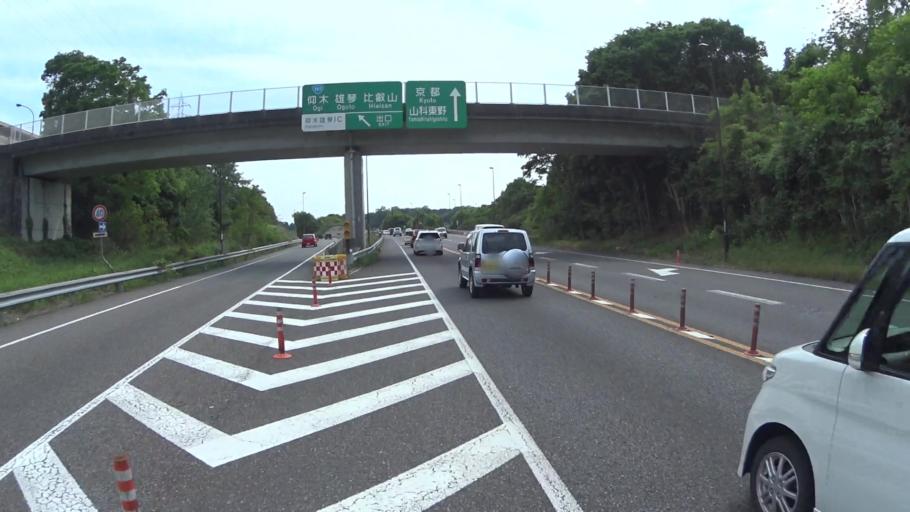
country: JP
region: Shiga Prefecture
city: Kitahama
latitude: 35.1012
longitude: 135.8928
